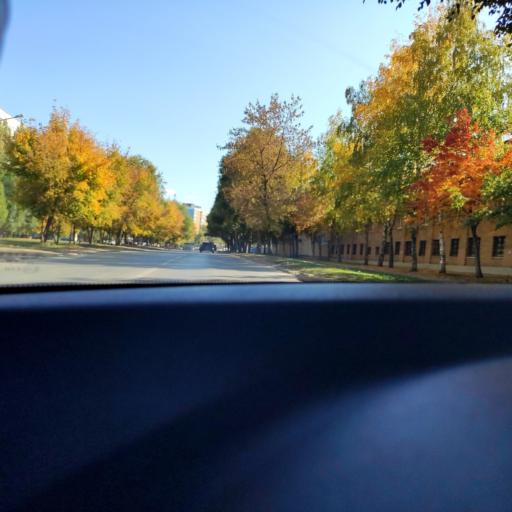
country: RU
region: Samara
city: Samara
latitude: 53.2449
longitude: 50.2061
